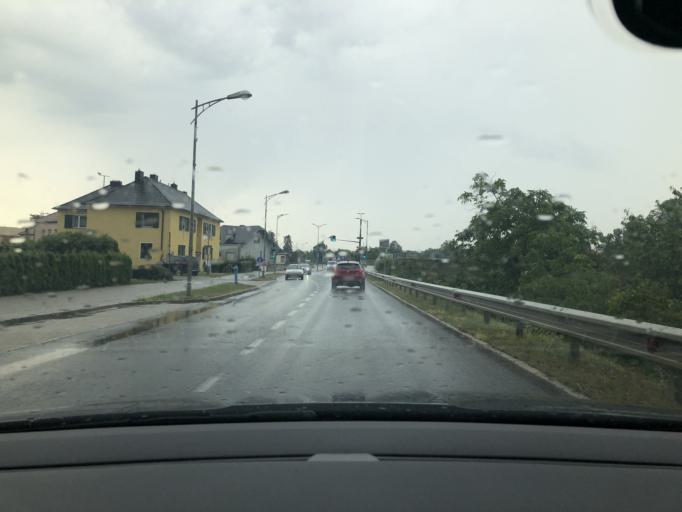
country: AT
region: Lower Austria
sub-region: Politischer Bezirk Ganserndorf
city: Ganserndorf
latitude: 48.3373
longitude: 16.7203
